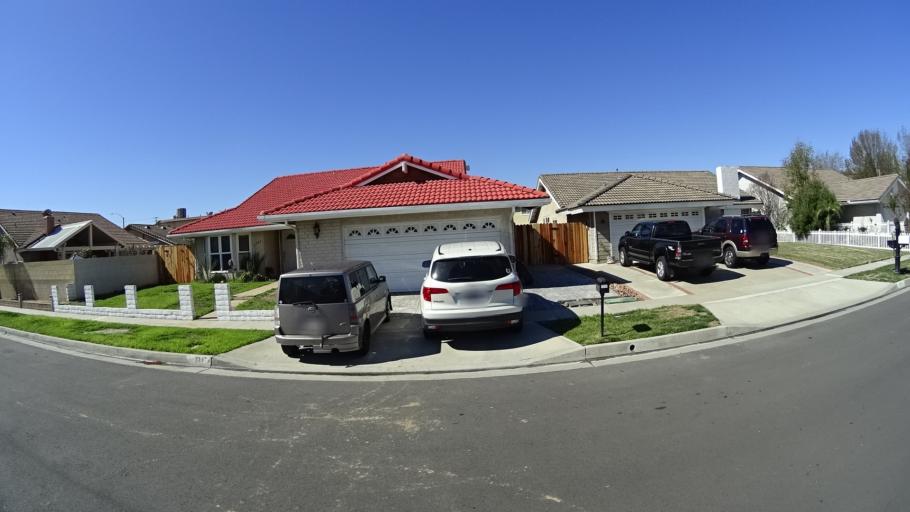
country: US
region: California
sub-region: Orange County
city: Yorba Linda
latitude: 33.8682
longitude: -117.8160
